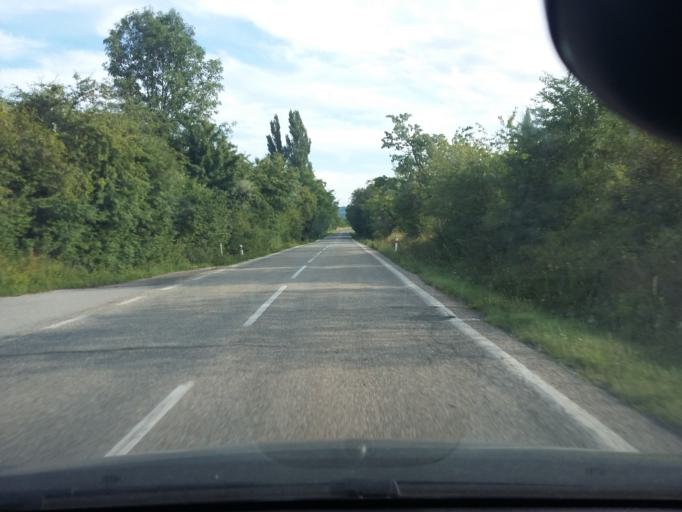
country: SK
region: Bratislavsky
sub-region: Okres Malacky
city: Malacky
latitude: 48.4332
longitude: 17.1595
